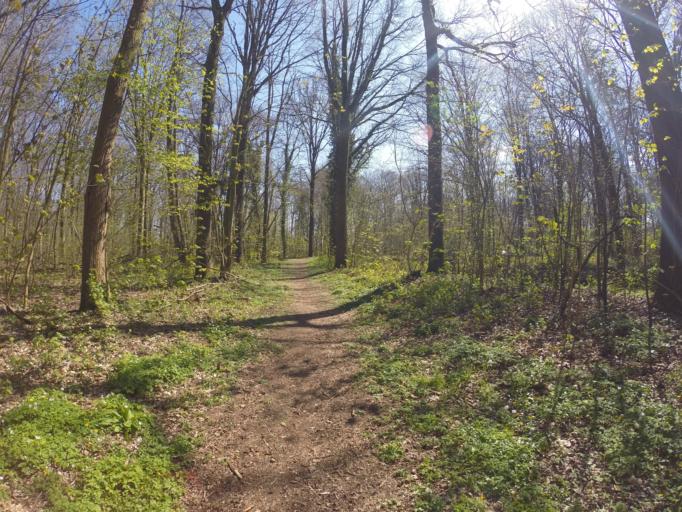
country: BE
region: Flanders
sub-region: Provincie West-Vlaanderen
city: Oostkamp
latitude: 51.1468
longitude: 3.2531
